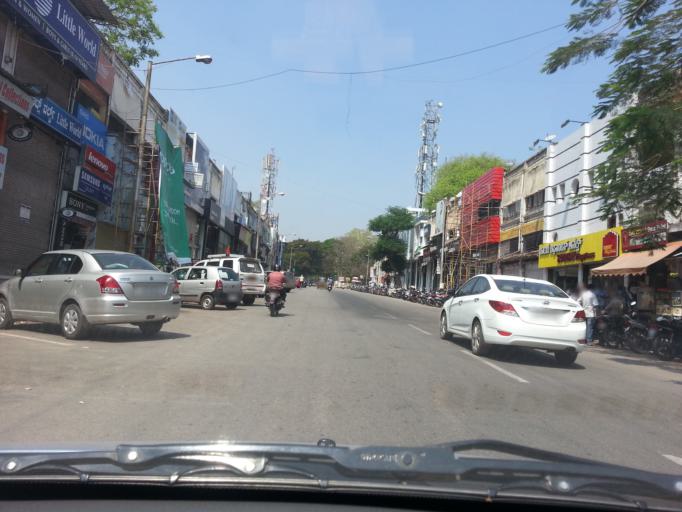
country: IN
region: Karnataka
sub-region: Mysore
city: Mysore
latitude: 12.3095
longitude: 76.6459
